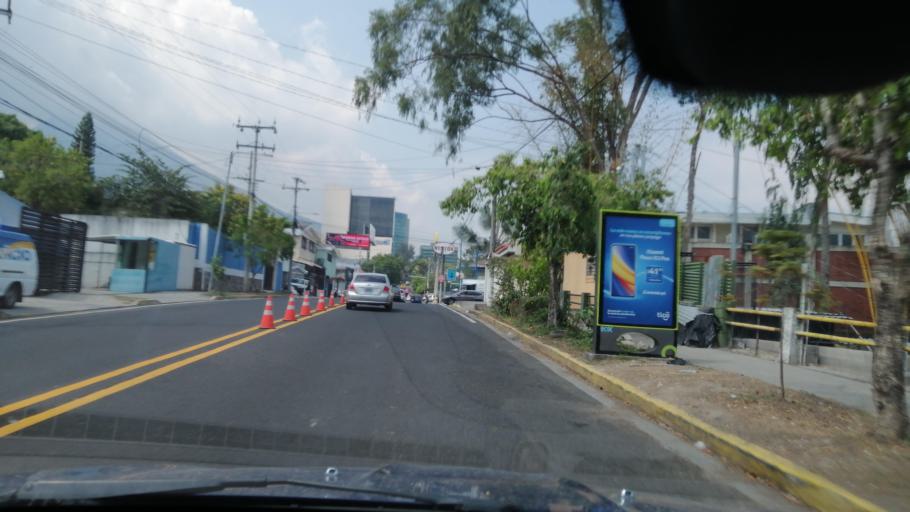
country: SV
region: La Libertad
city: Antiguo Cuscatlan
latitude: 13.7007
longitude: -89.2412
